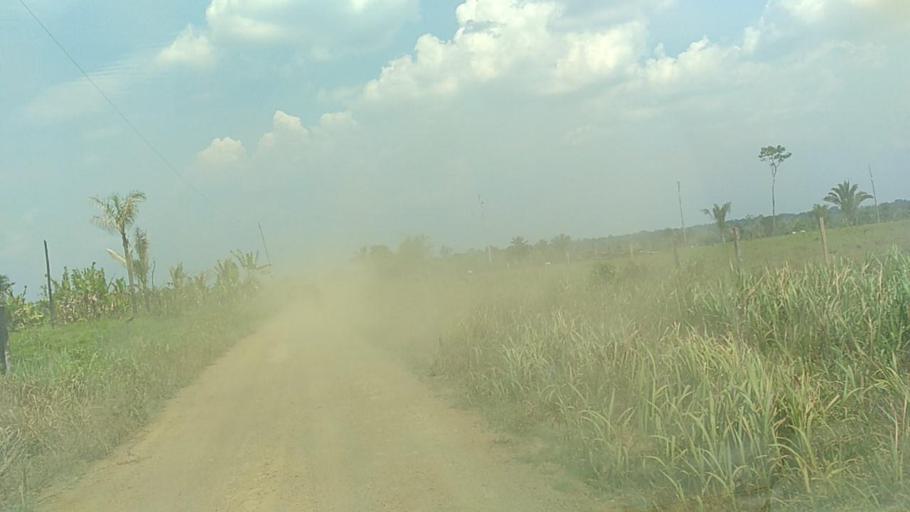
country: BR
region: Rondonia
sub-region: Porto Velho
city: Porto Velho
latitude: -8.6473
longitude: -64.1733
